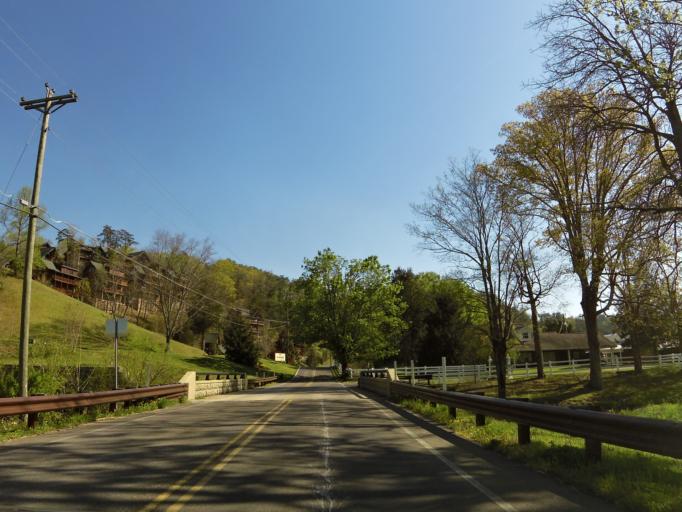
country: US
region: Tennessee
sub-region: Sevier County
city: Pigeon Forge
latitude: 35.7856
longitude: -83.6266
